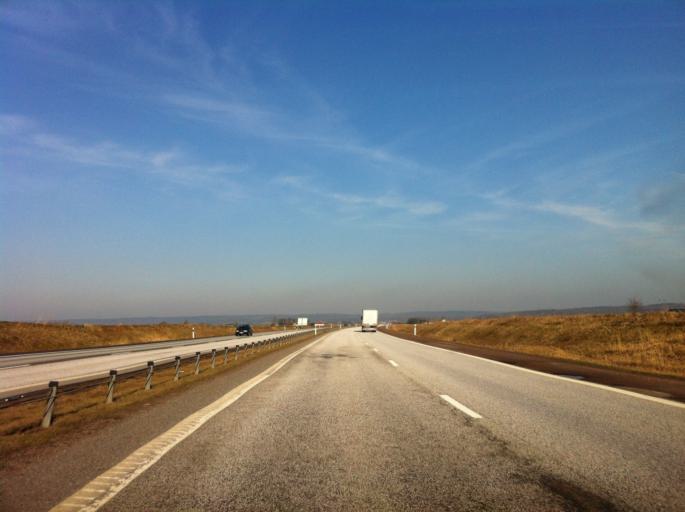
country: SE
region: Skane
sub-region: Angelholms Kommun
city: AEngelholm
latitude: 56.2720
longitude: 12.8943
